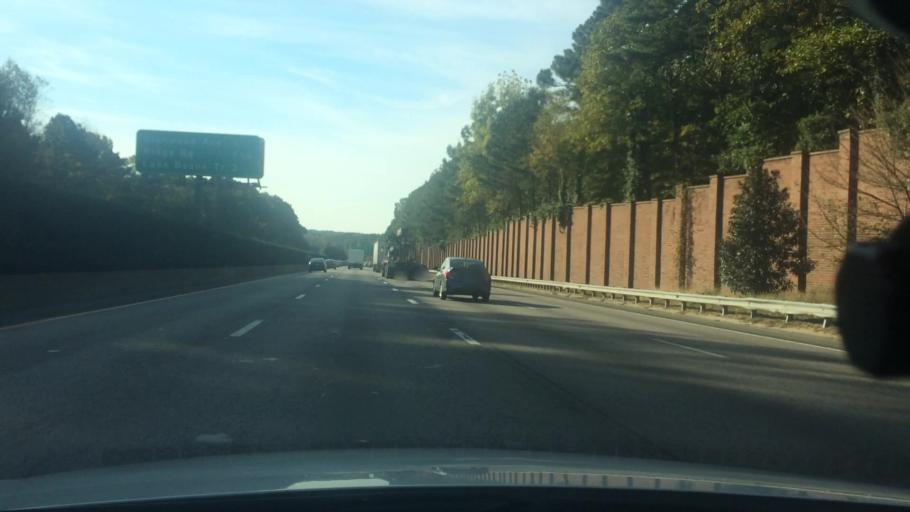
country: US
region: North Carolina
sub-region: Wake County
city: West Raleigh
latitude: 35.8363
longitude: -78.6530
